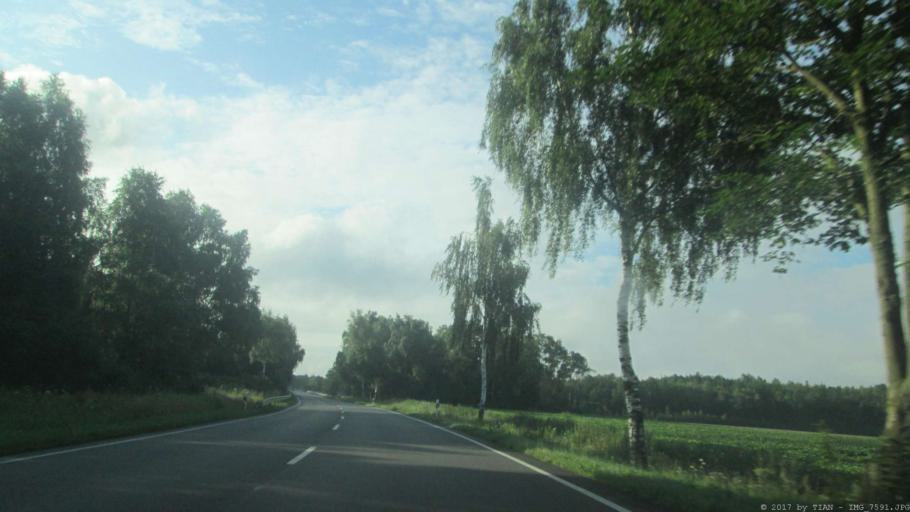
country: DE
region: Lower Saxony
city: Wrestedt
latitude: 52.9285
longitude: 10.6024
